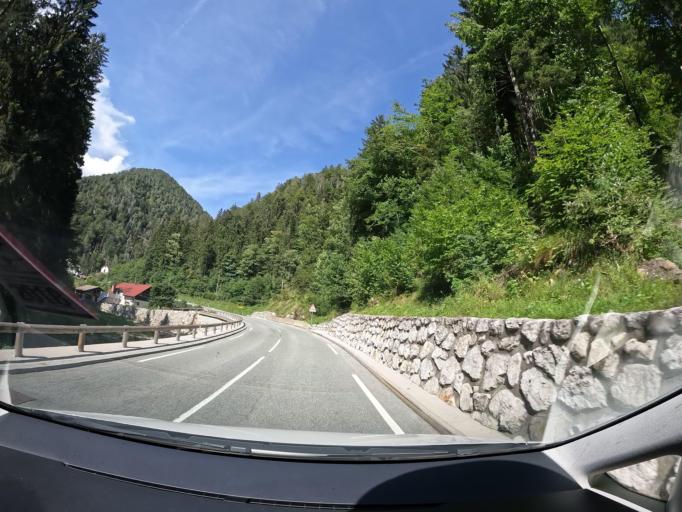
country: SI
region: Trzic
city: Trzic
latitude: 46.4061
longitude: 14.3162
